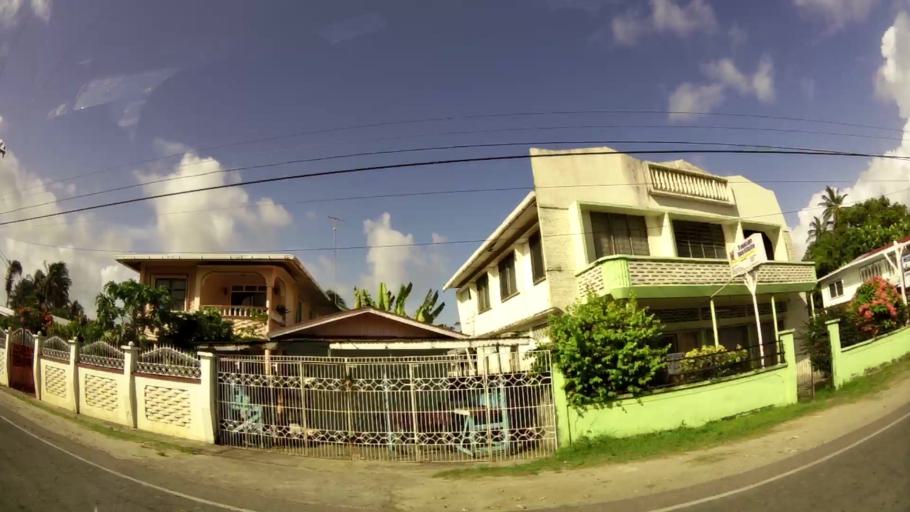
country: GY
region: Demerara-Mahaica
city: Mahaica Village
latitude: 6.7534
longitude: -57.9743
